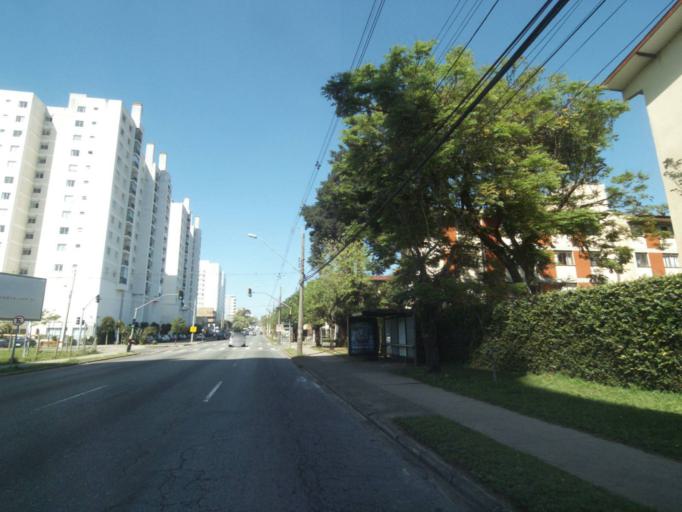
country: BR
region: Parana
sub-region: Curitiba
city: Curitiba
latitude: -25.3880
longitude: -49.2369
